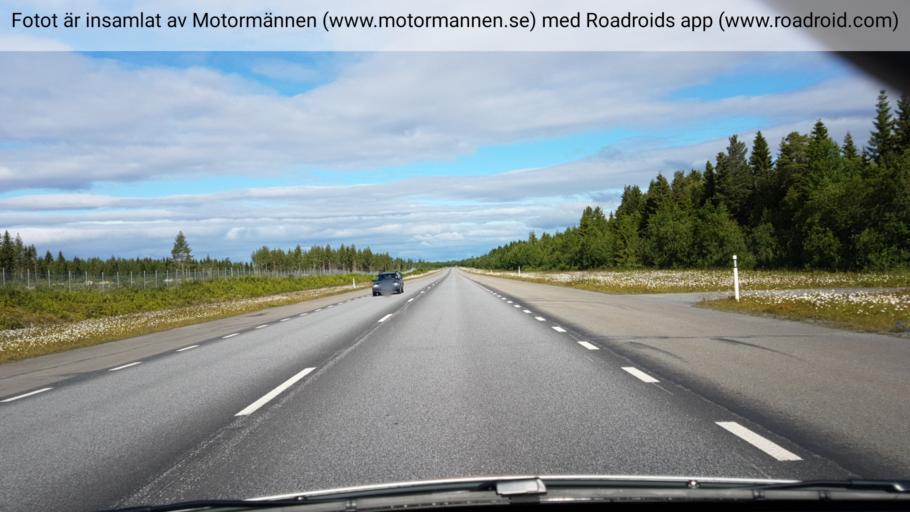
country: SE
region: Jaemtland
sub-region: OEstersunds Kommun
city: Ostersund
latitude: 63.1952
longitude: 14.5185
